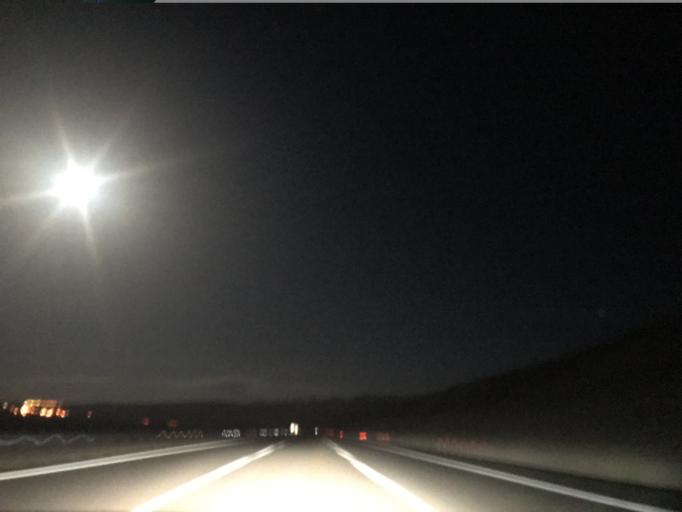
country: TR
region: Nigde
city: Ulukisla
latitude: 37.6336
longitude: 34.4494
